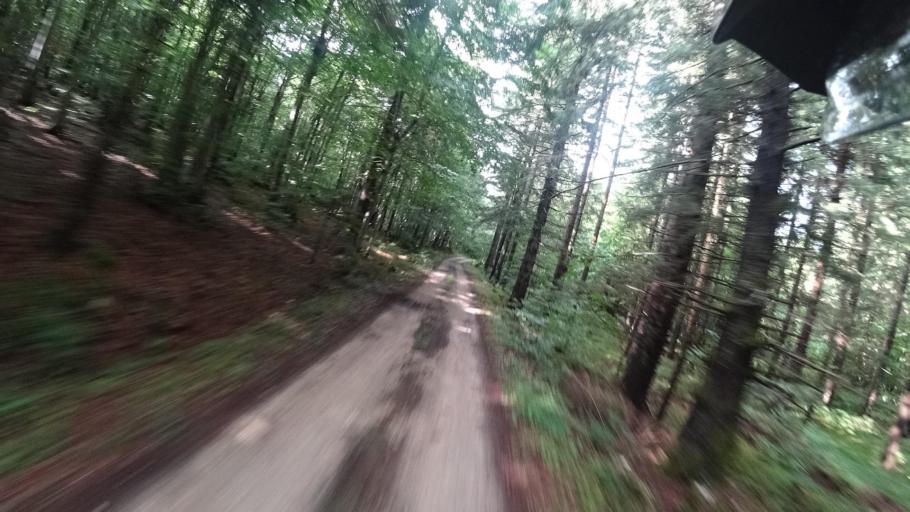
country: HR
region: Licko-Senjska
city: Jezerce
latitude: 44.7754
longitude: 15.6472
